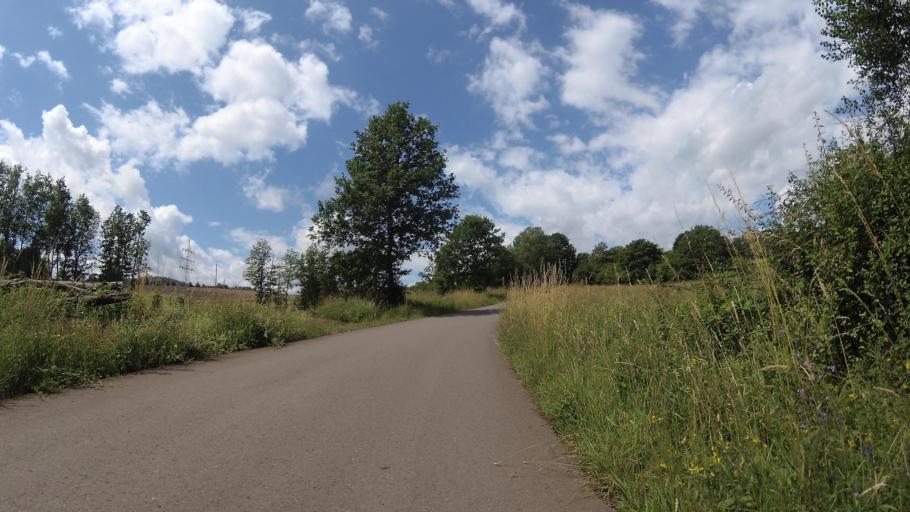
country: DE
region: Saarland
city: Tholey
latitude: 49.5039
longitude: 7.0459
